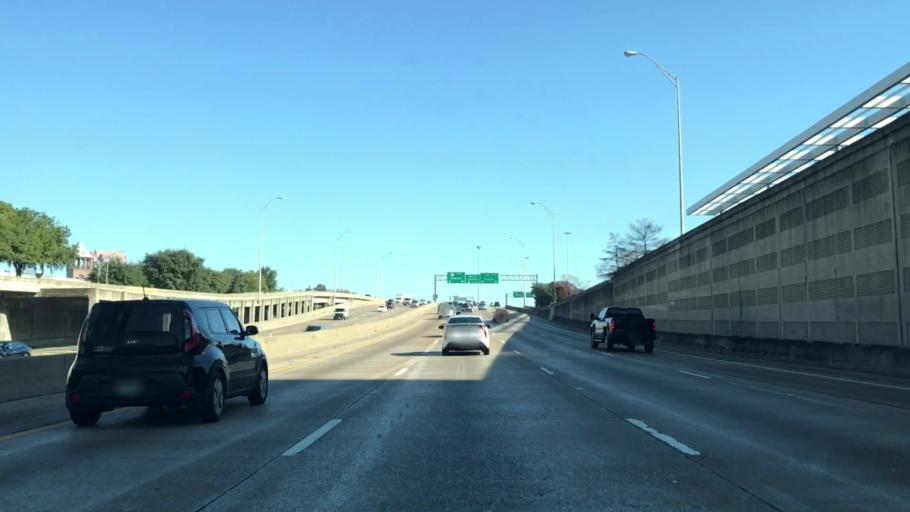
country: US
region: Texas
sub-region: Dallas County
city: Dallas
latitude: 32.7909
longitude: -96.7996
